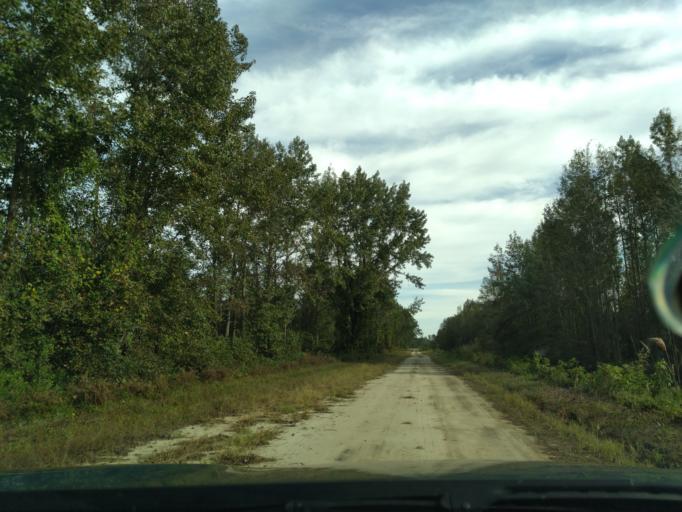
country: US
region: North Carolina
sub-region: Beaufort County
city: Belhaven
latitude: 35.6931
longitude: -76.5547
